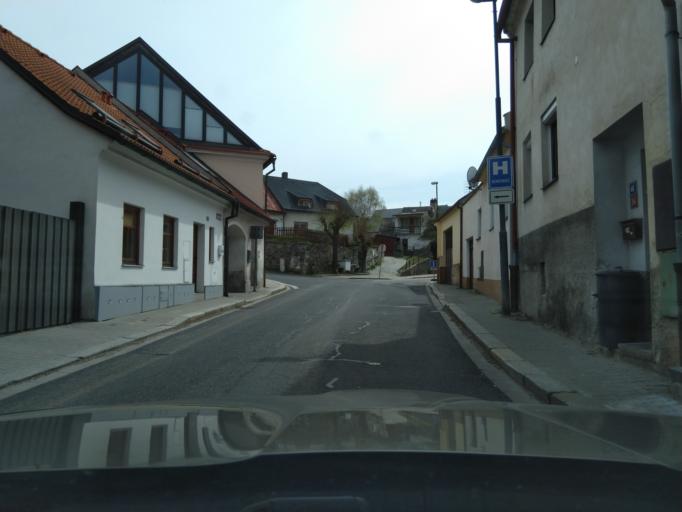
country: CZ
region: Plzensky
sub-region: Okres Klatovy
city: Susice
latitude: 49.2287
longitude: 13.5256
